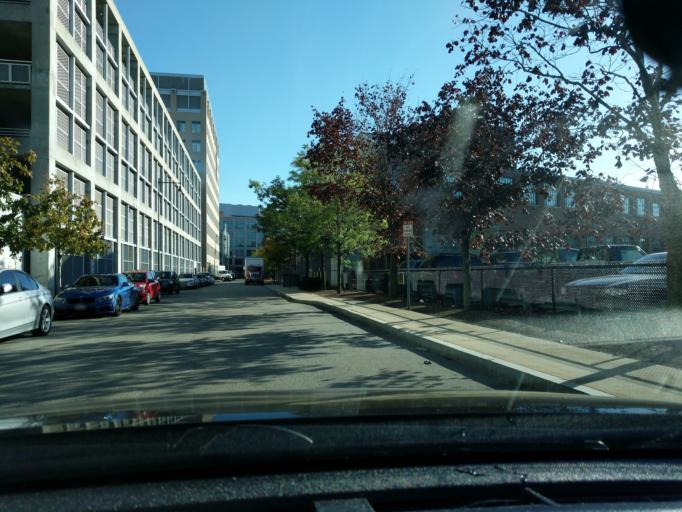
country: US
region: Massachusetts
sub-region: Middlesex County
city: Cambridge
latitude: 42.3595
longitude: -71.1008
